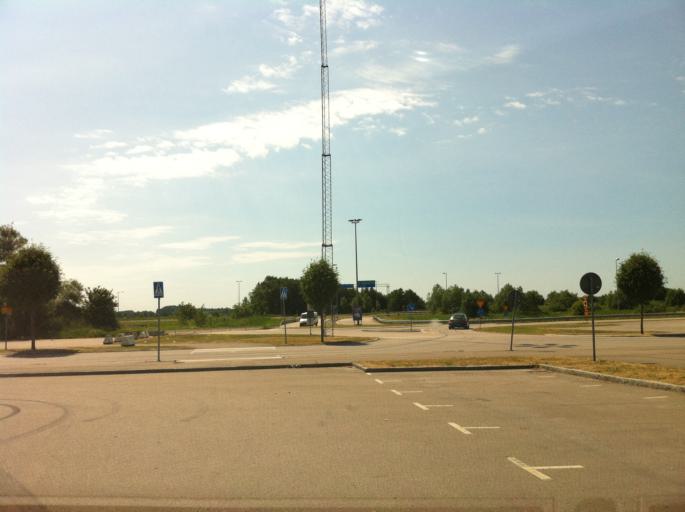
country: SE
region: Skane
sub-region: Helsingborg
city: Hyllinge
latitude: 56.0979
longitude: 12.8602
